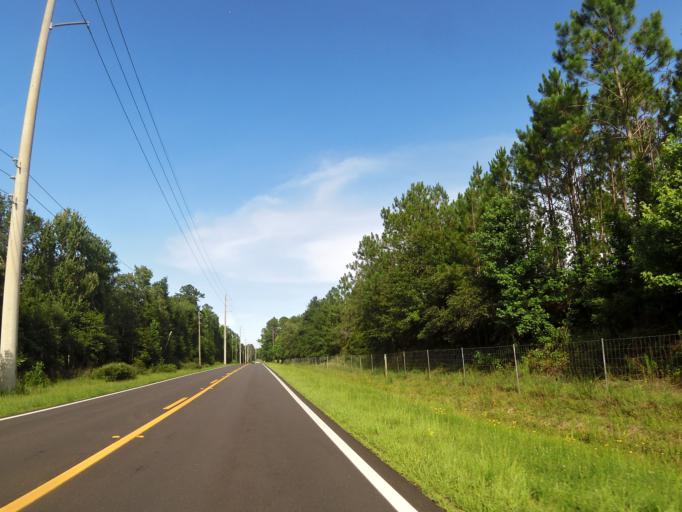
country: US
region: Florida
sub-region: Clay County
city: Green Cove Springs
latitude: 30.0148
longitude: -81.5716
